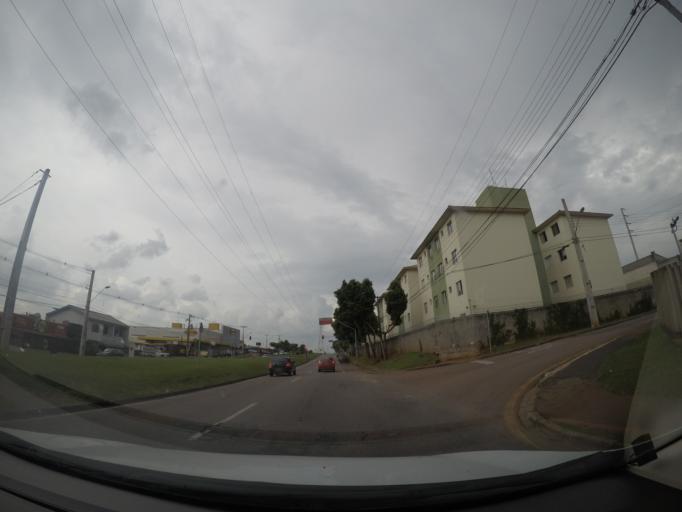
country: BR
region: Parana
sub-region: Sao Jose Dos Pinhais
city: Sao Jose dos Pinhais
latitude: -25.5434
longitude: -49.2685
